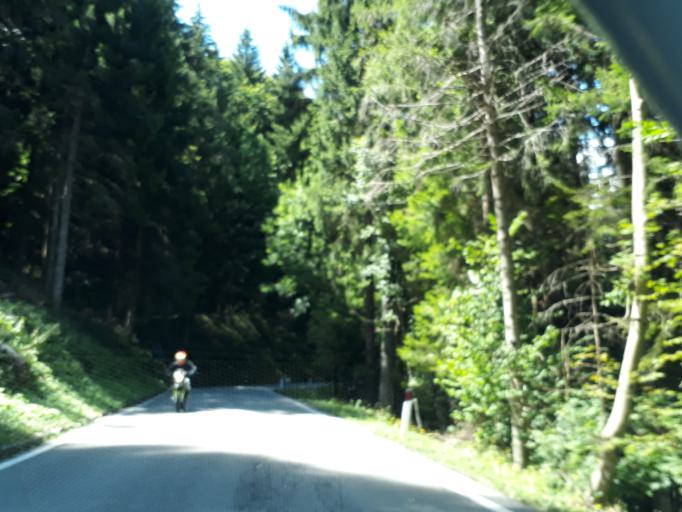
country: IT
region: Trentino-Alto Adige
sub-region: Provincia di Trento
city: Cimego
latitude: 45.8676
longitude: 10.6633
